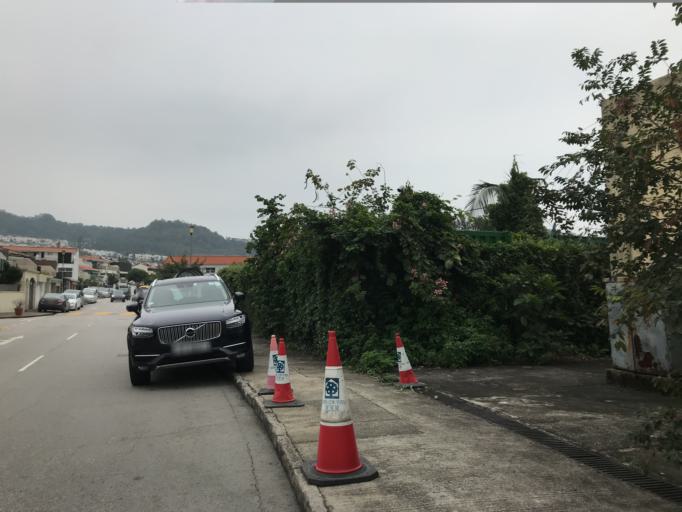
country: HK
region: Tai Po
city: Tai Po
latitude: 22.4648
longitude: 114.1527
